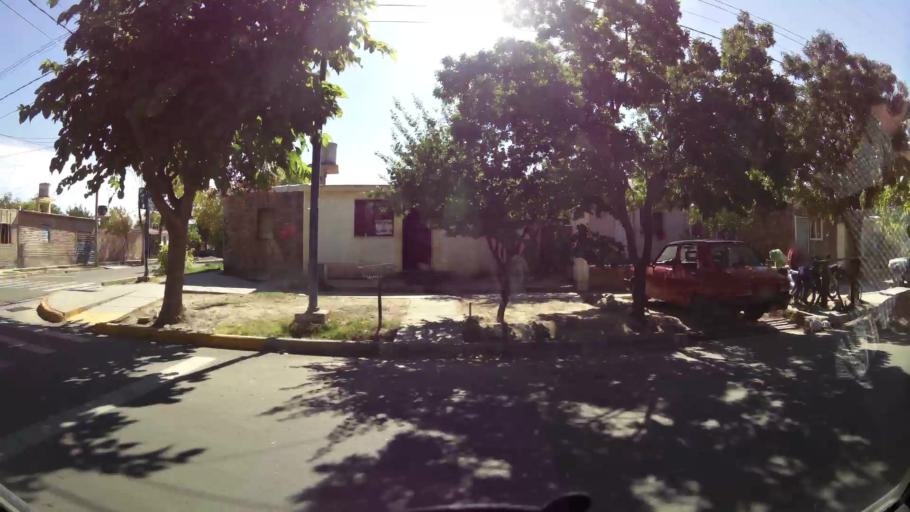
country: AR
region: Mendoza
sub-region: Departamento de Godoy Cruz
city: Godoy Cruz
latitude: -32.9507
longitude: -68.8230
